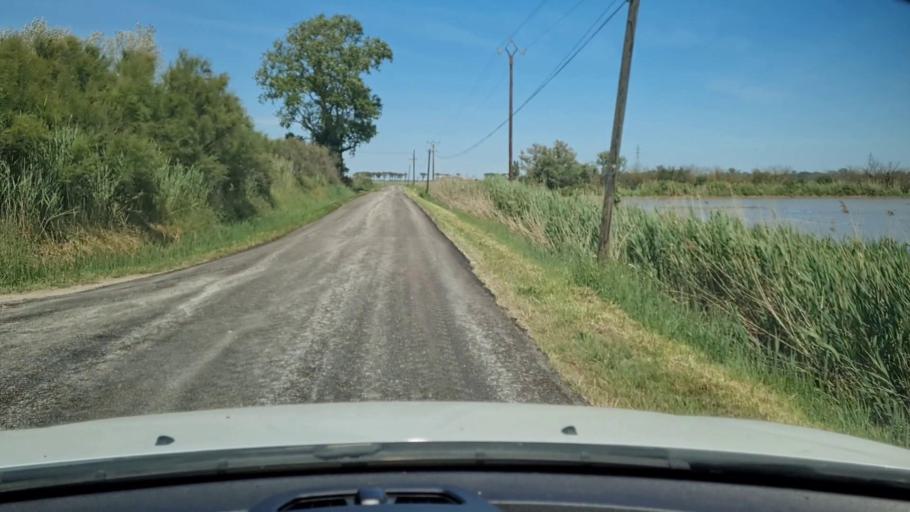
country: FR
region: Languedoc-Roussillon
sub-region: Departement du Gard
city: Saint-Gilles
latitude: 43.5675
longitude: 4.3927
